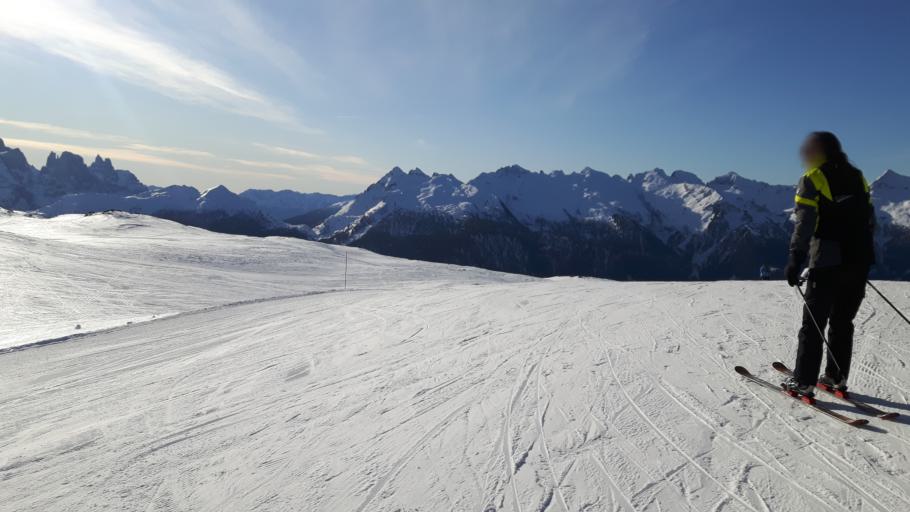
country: IT
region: Trentino-Alto Adige
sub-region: Provincia di Trento
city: Moena
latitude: 46.3448
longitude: 11.7213
